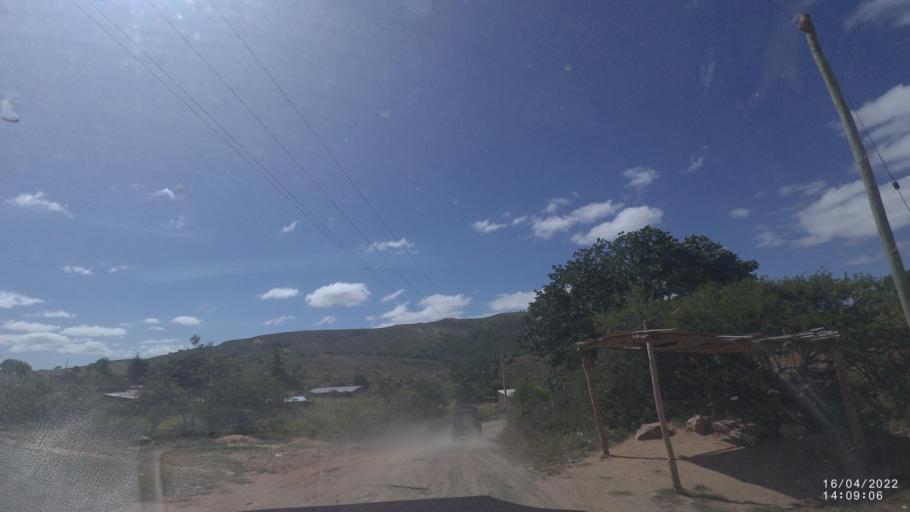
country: BO
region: Cochabamba
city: Mizque
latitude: -18.0616
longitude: -65.5233
